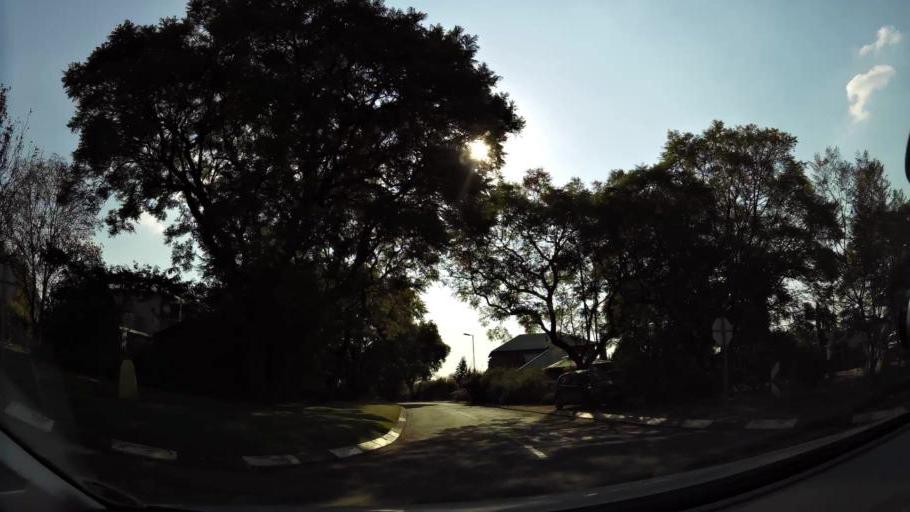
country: ZA
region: Gauteng
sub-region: City of Johannesburg Metropolitan Municipality
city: Modderfontein
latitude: -26.1026
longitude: 28.1487
